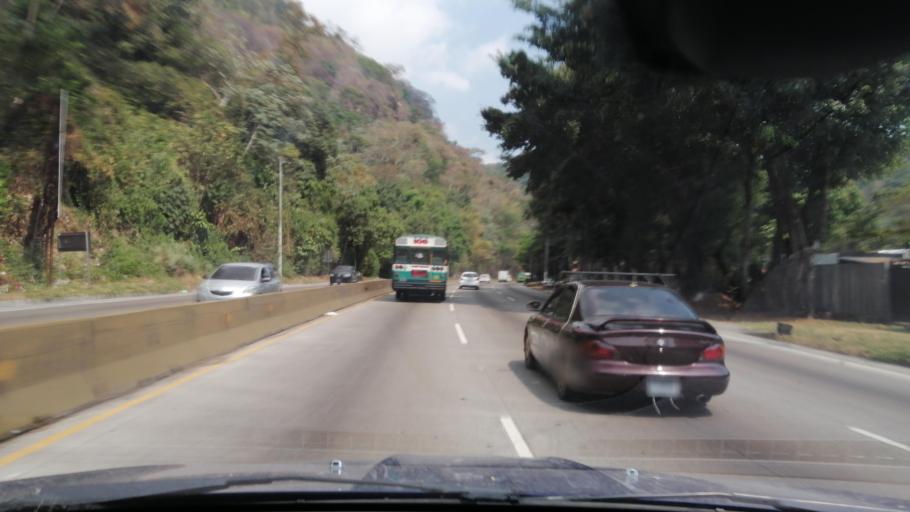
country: SV
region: La Libertad
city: Santa Tecla
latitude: 13.6988
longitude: -89.3261
